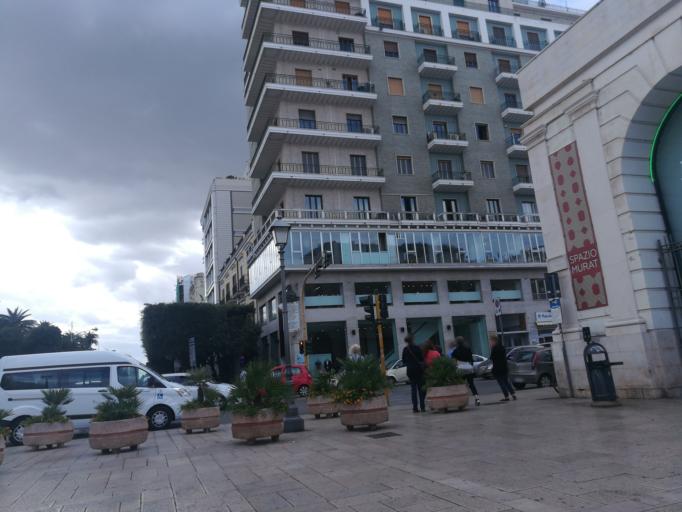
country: IT
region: Apulia
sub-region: Provincia di Bari
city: Bari
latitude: 41.1264
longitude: 16.8719
